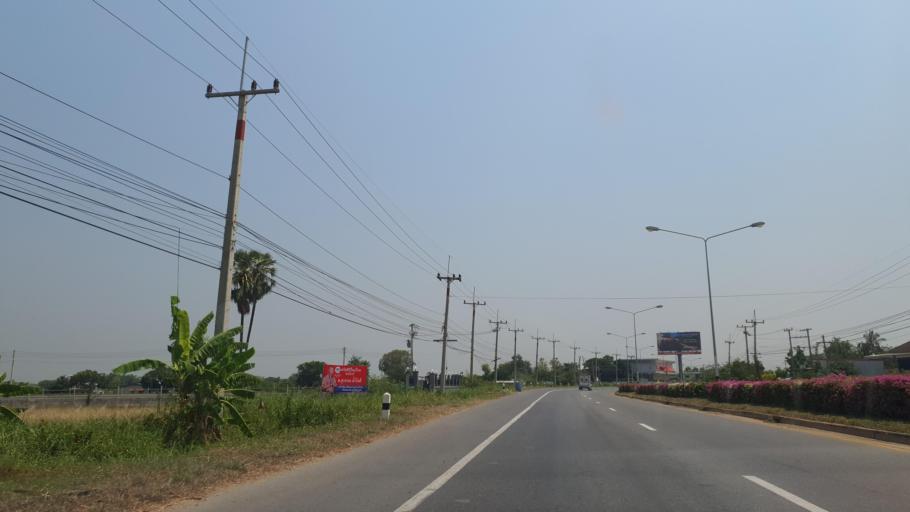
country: TH
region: Kanchanaburi
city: Phanom Thuan
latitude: 14.2421
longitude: 99.8075
